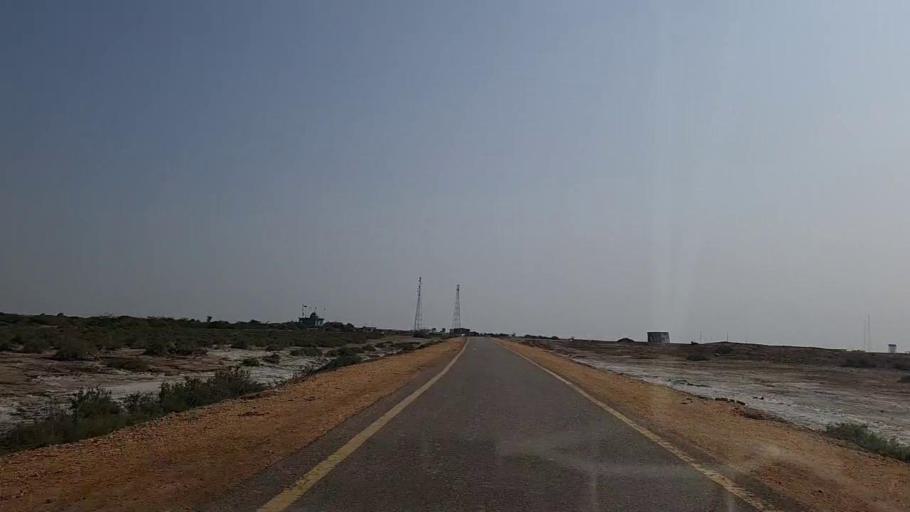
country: PK
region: Sindh
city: Chuhar Jamali
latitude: 24.1687
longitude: 67.8956
